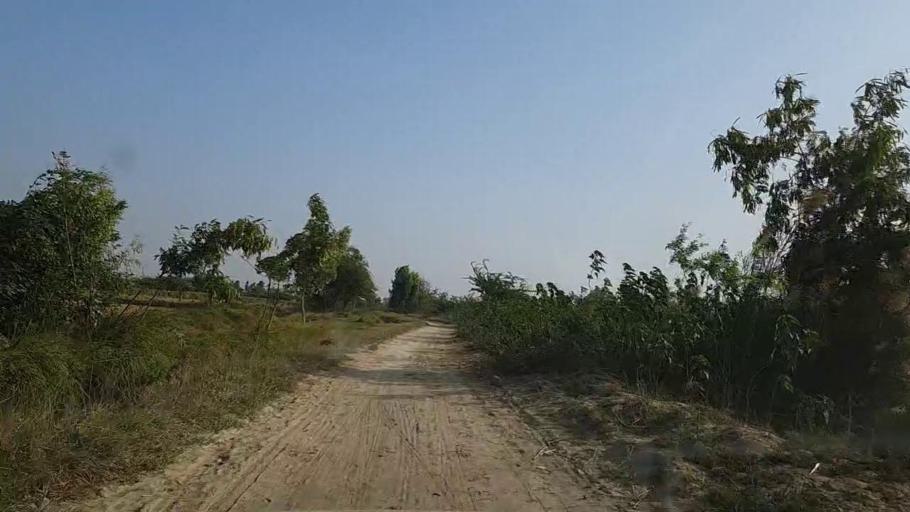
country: PK
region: Sindh
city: Mirpur Sakro
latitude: 24.5889
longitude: 67.6475
